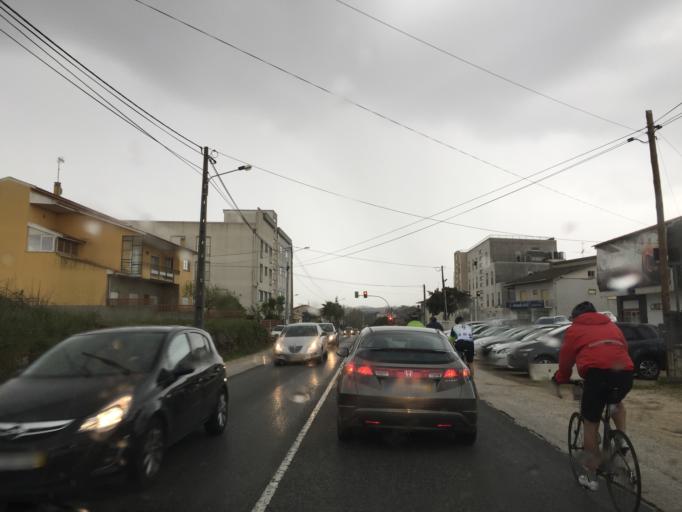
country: PT
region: Leiria
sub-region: Leiria
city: Santa Catarina da Serra
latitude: 39.6413
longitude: -8.6851
